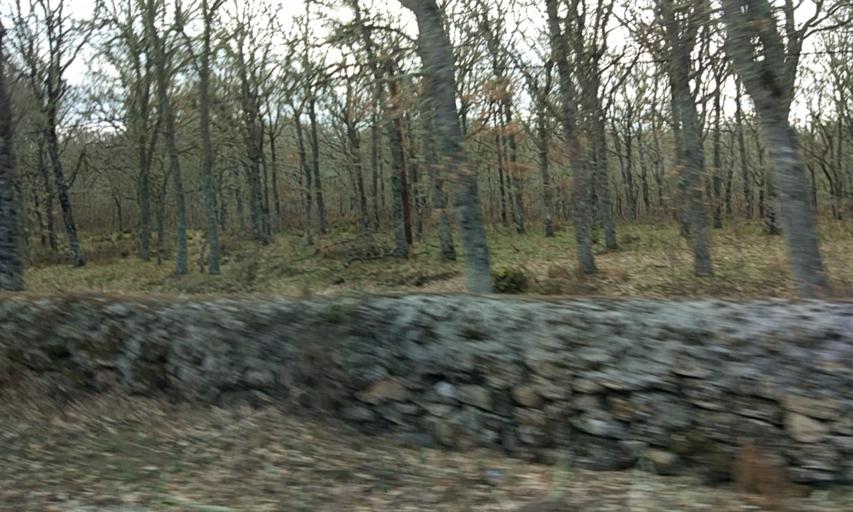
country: ES
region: Castille and Leon
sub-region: Provincia de Salamanca
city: Villasrubias
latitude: 40.3177
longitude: -6.6472
